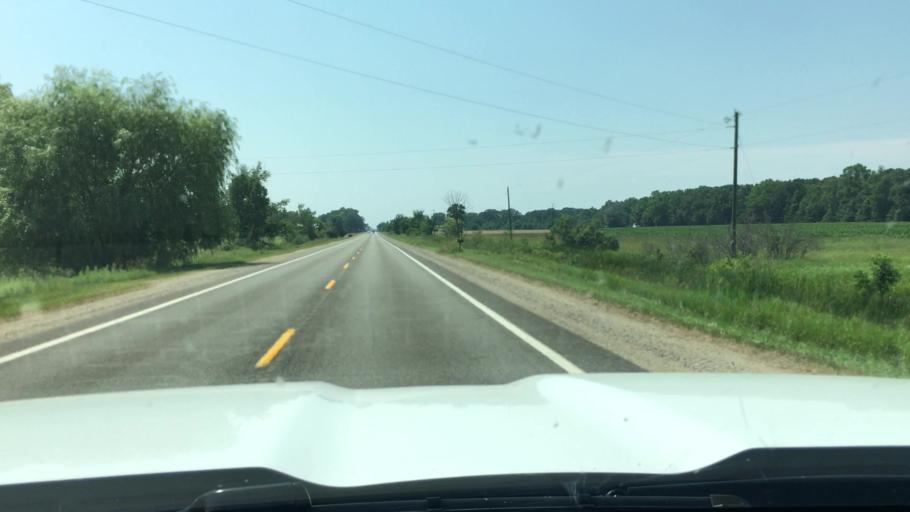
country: US
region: Michigan
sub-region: Clinton County
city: Ovid
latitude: 43.1760
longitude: -84.3989
